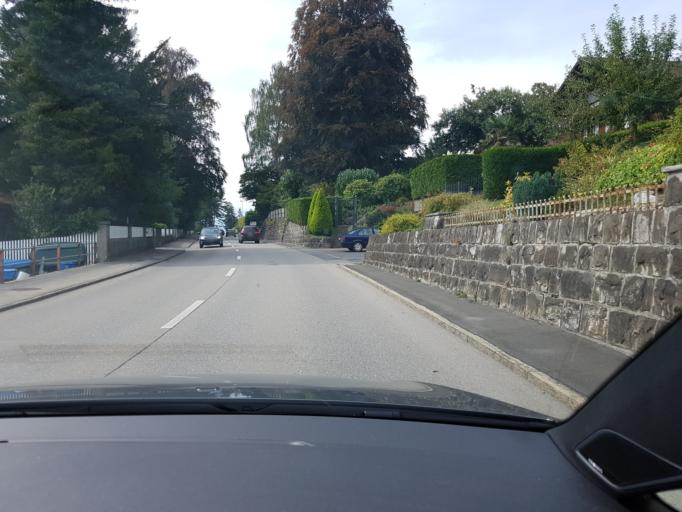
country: CH
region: Bern
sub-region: Thun District
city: Sigriswil
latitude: 46.7163
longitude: 7.6914
